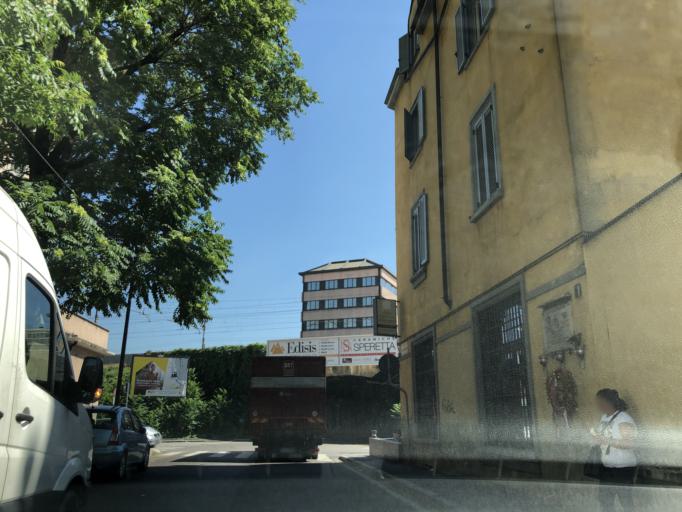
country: IT
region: Lombardy
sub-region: Citta metropolitana di Milano
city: Cormano
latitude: 45.5087
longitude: 9.1678
